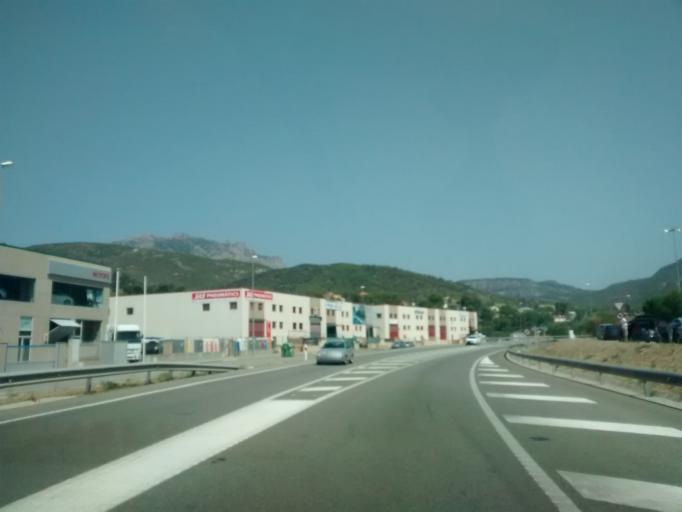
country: ES
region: Catalonia
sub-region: Provincia de Barcelona
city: Olesa de Montserrat
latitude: 41.5531
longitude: 1.8792
